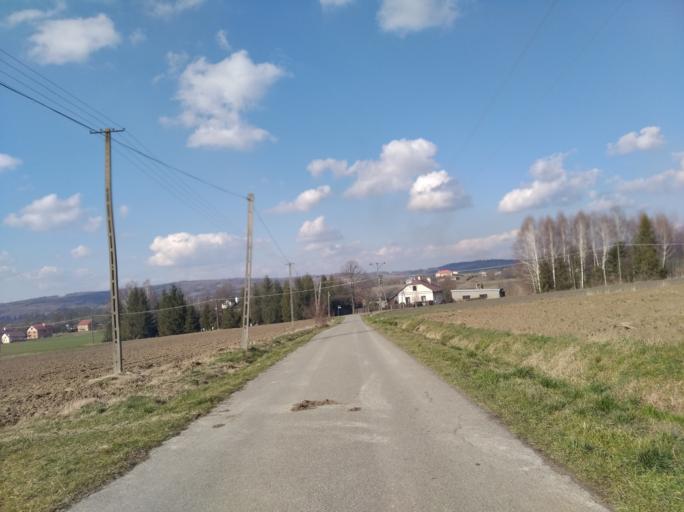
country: PL
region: Subcarpathian Voivodeship
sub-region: Powiat strzyzowski
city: Wysoka Strzyzowska
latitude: 49.8545
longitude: 21.7094
